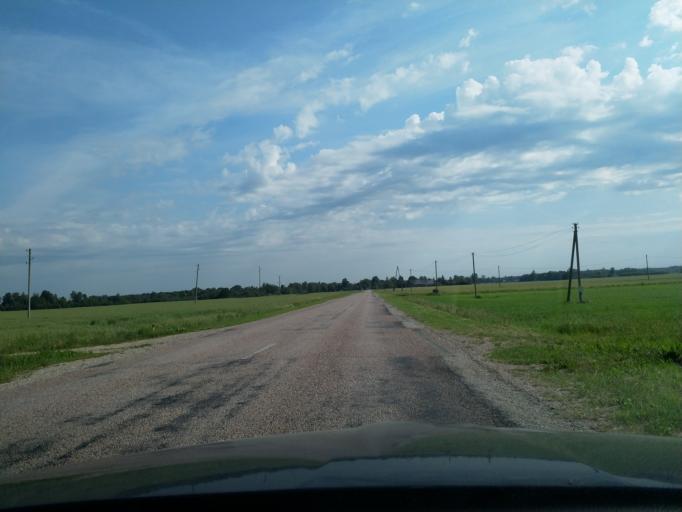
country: LV
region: Talsu Rajons
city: Sabile
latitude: 56.9539
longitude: 22.6094
